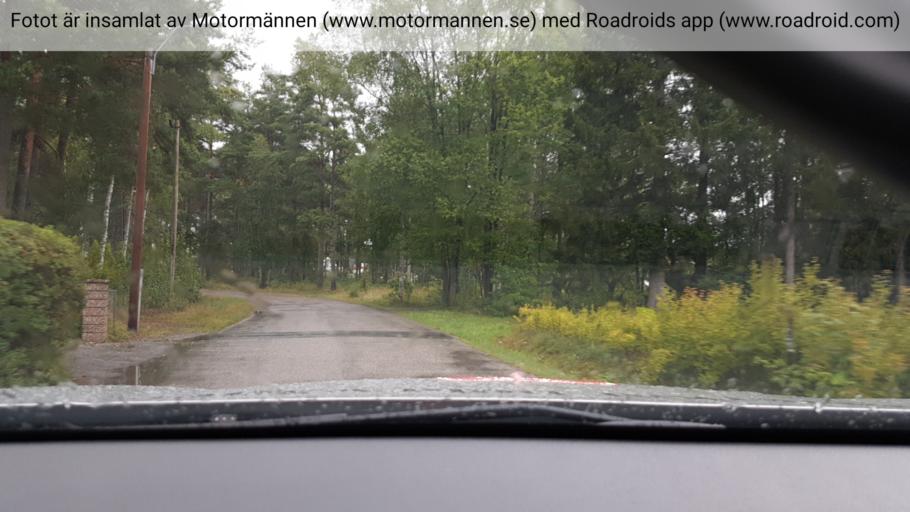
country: SE
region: Stockholm
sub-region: Haninge Kommun
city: Jordbro
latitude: 59.0961
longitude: 18.0417
